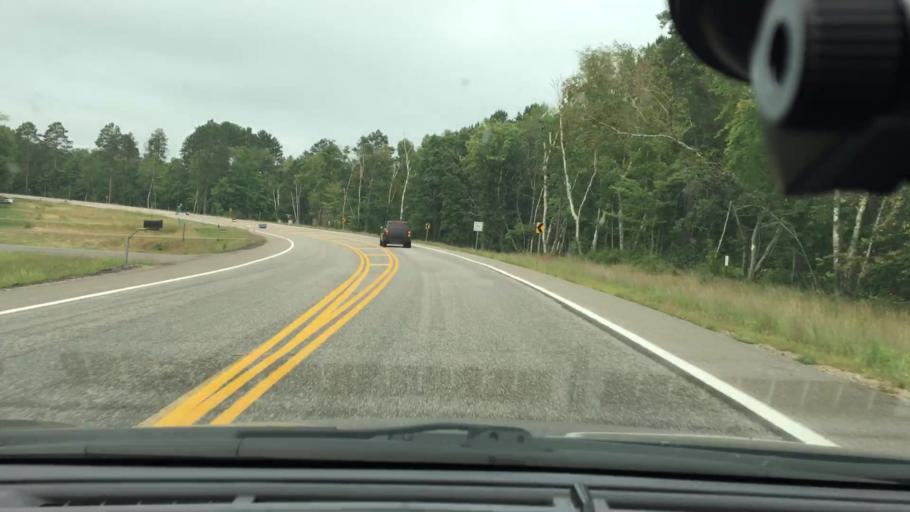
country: US
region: Minnesota
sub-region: Crow Wing County
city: Cross Lake
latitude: 46.6661
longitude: -94.0403
